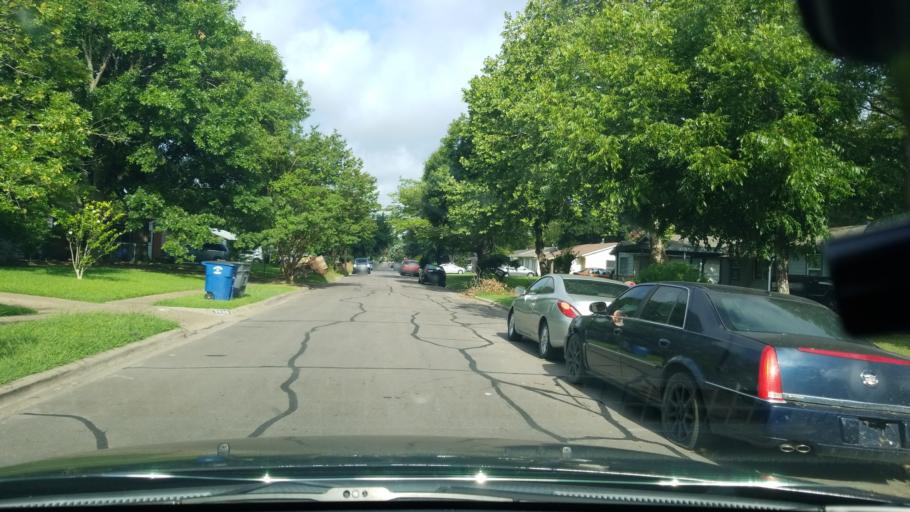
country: US
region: Texas
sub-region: Dallas County
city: Mesquite
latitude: 32.8189
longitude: -96.6714
